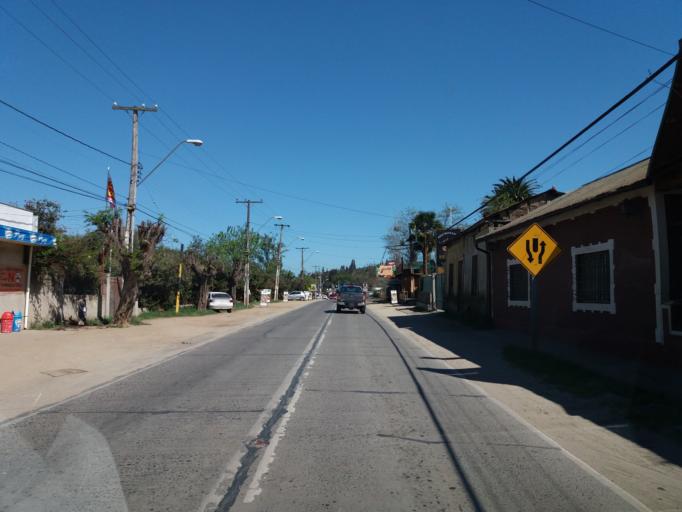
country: CL
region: Valparaiso
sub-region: Provincia de Marga Marga
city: Limache
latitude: -32.9958
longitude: -71.2303
